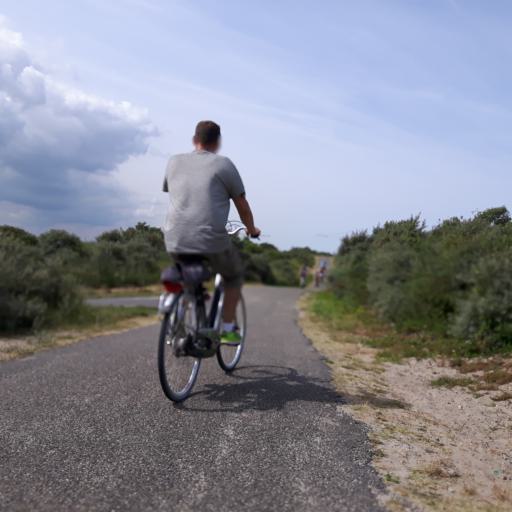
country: NL
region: Zeeland
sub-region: Gemeente Sluis
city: Sluis
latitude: 51.3837
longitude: 3.4077
